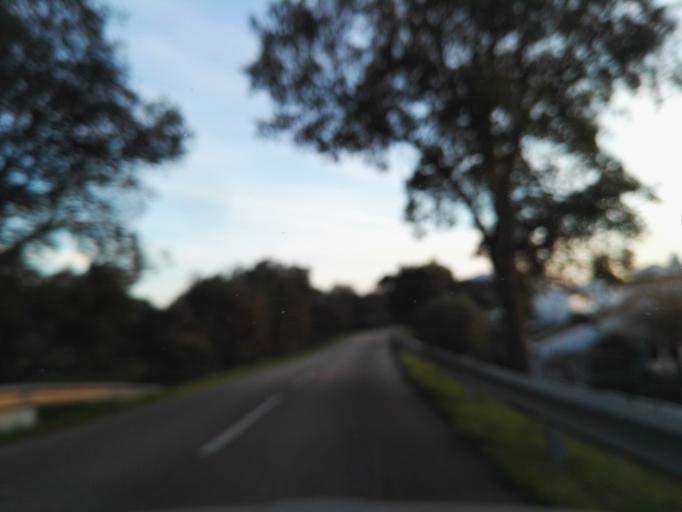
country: PT
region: Evora
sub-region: Montemor-O-Novo
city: Montemor-o-Novo
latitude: 38.7652
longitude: -8.1931
